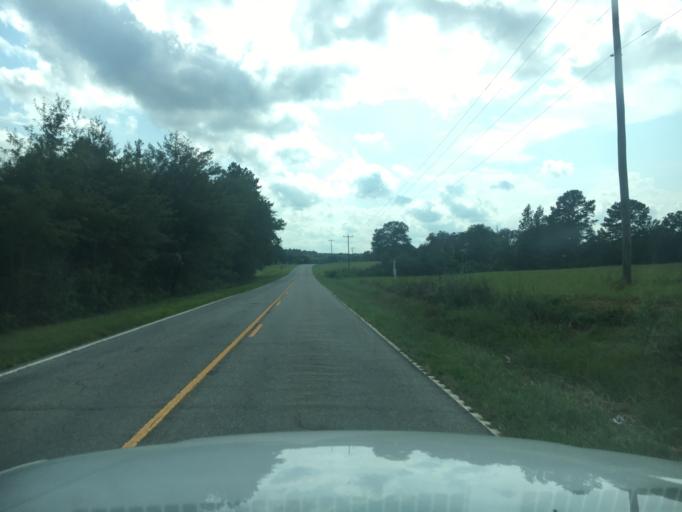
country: US
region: South Carolina
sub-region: Anderson County
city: Belton
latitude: 34.5384
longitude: -82.4493
